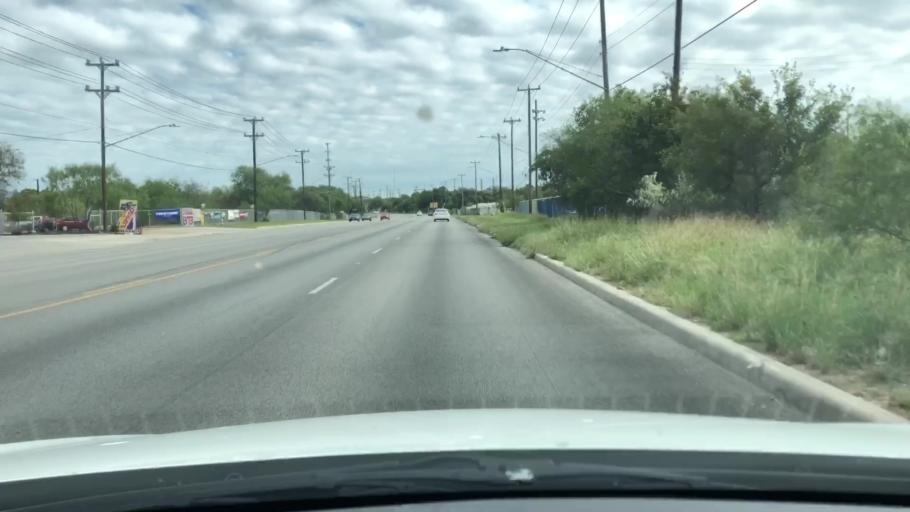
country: US
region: Texas
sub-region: Bexar County
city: Leon Valley
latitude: 29.4786
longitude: -98.6552
